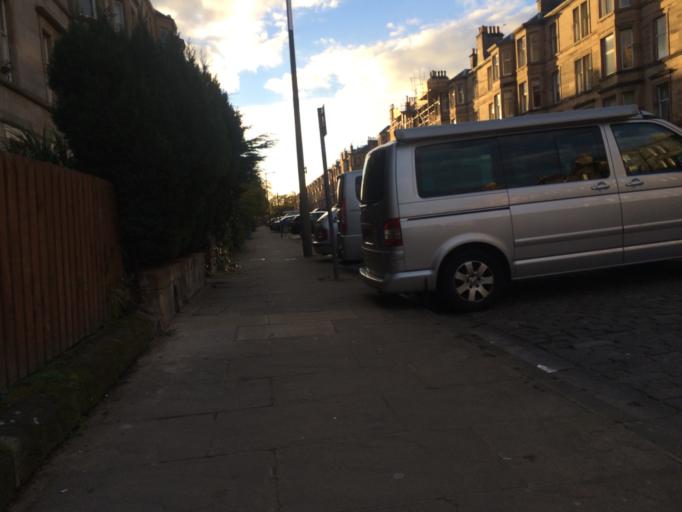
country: GB
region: Scotland
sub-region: Edinburgh
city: Edinburgh
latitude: 55.9354
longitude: -3.1952
